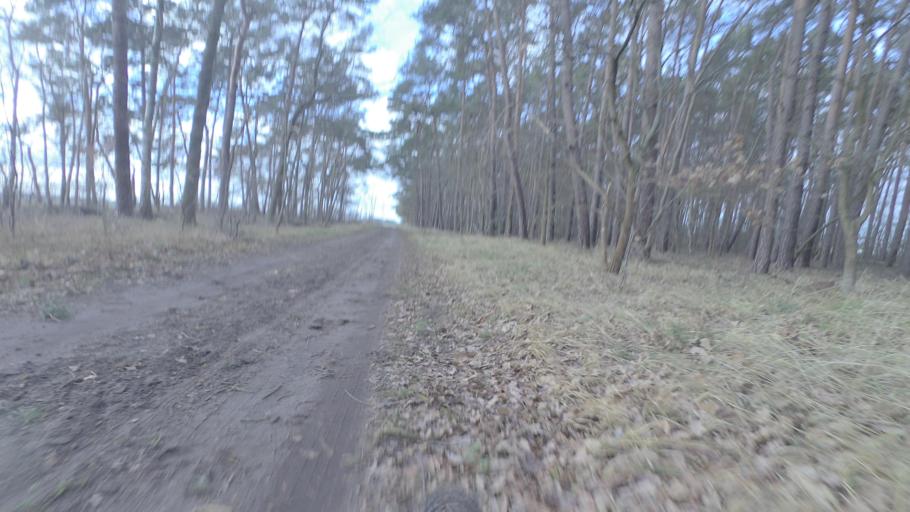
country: DE
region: Brandenburg
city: Trebbin
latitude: 52.2279
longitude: 13.3025
